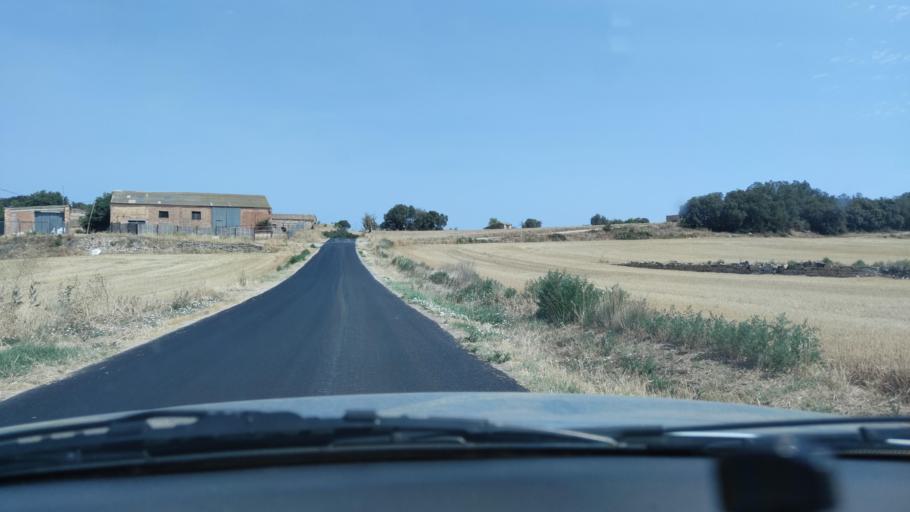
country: ES
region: Catalonia
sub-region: Provincia de Lleida
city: Ivorra
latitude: 41.7659
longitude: 1.3261
